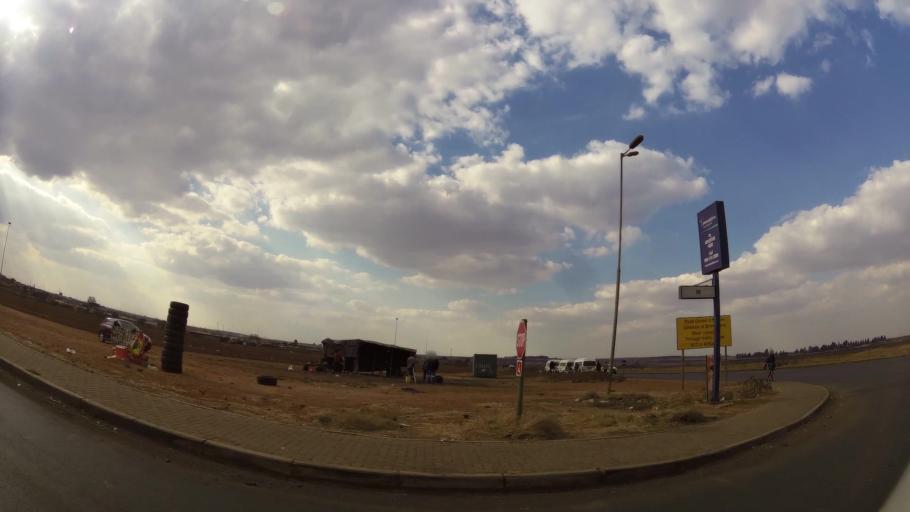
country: ZA
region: Mpumalanga
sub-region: Nkangala District Municipality
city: Delmas
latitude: -26.1467
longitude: 28.6912
